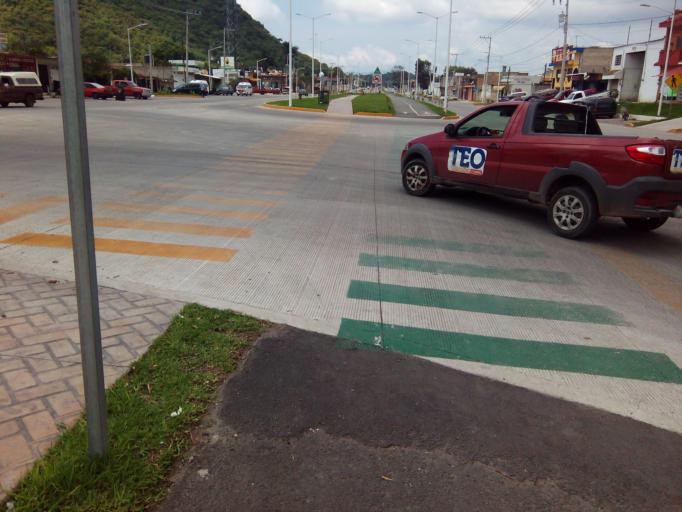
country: MX
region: Nayarit
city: Tepic
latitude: 21.5369
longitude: -104.8710
